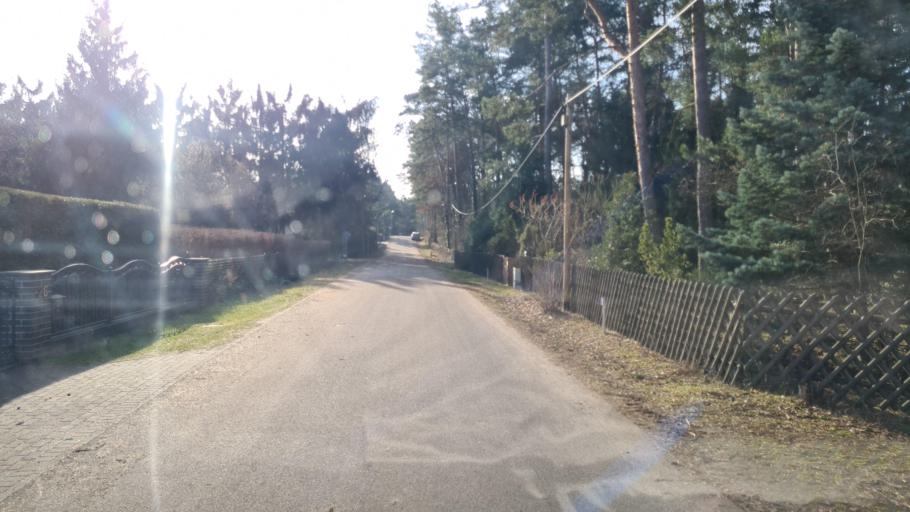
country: DE
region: Brandenburg
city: Gross Koris
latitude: 52.1625
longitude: 13.6890
